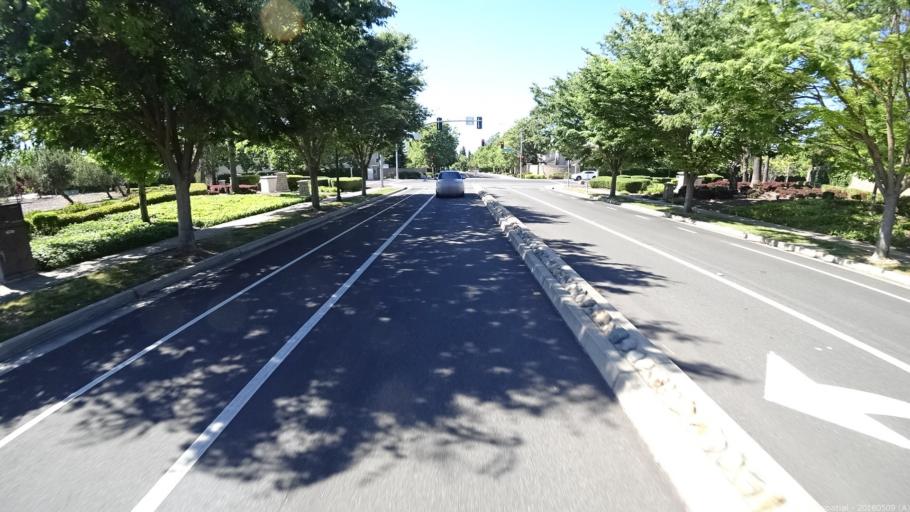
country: US
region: California
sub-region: Sacramento County
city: Elverta
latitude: 38.6733
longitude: -121.5191
